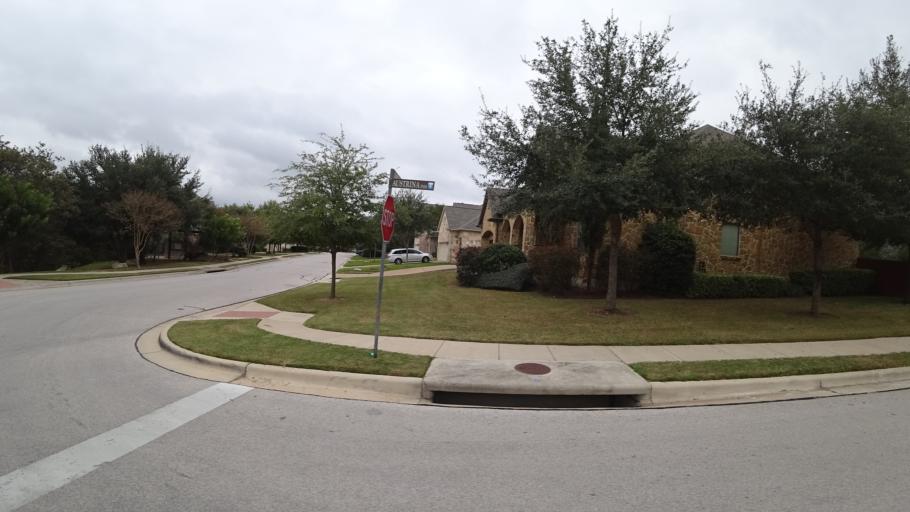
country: US
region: Texas
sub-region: Travis County
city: Hudson Bend
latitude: 30.3615
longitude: -97.9069
